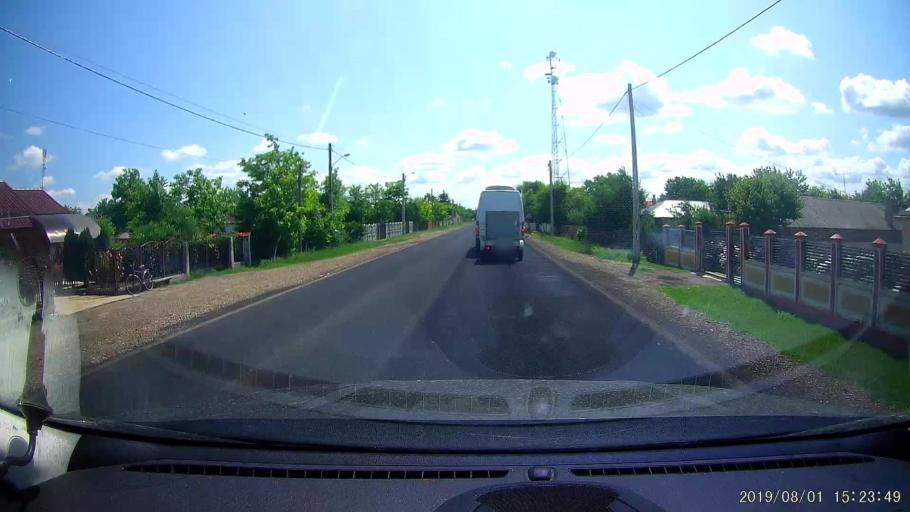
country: RO
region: Braila
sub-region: Comuna Viziru
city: Lanurile
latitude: 45.0376
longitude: 27.7555
